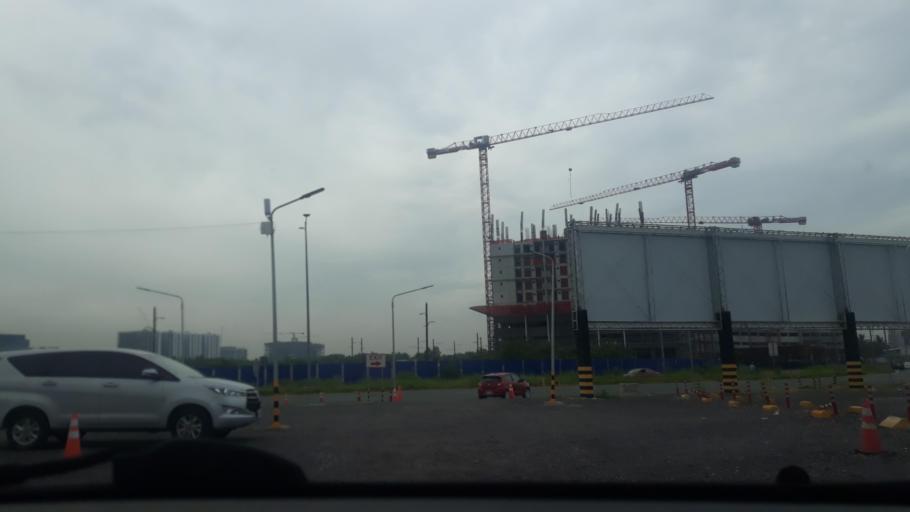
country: PH
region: Metro Manila
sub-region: Makati City
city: Makati City
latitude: 14.5179
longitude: 120.9854
